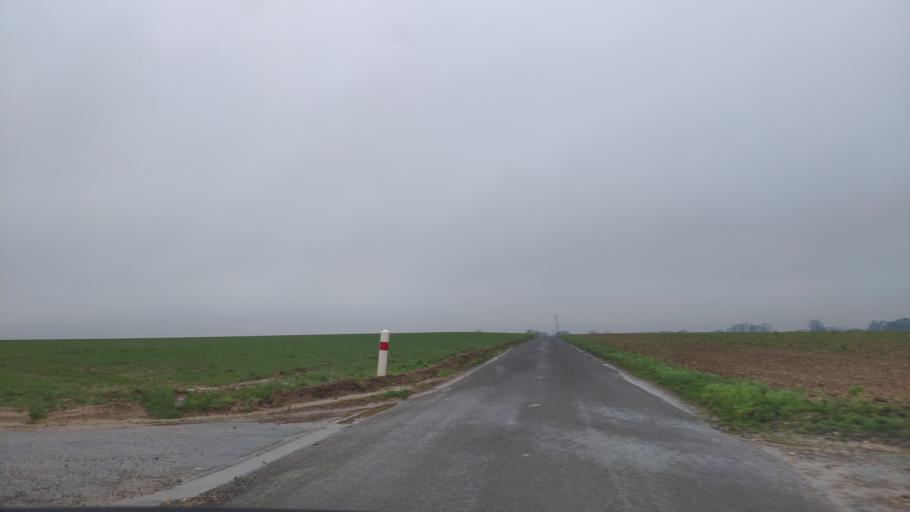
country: FR
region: Haute-Normandie
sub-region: Departement de la Seine-Maritime
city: Neville
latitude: 49.7928
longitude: 0.7078
